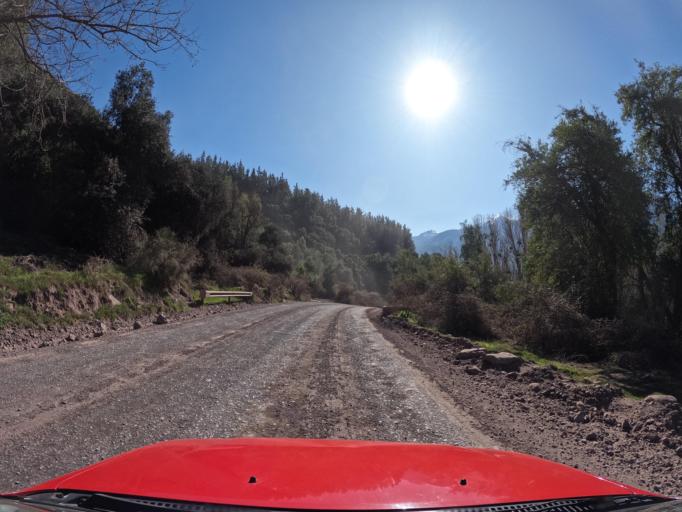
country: CL
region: O'Higgins
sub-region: Provincia de Colchagua
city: Chimbarongo
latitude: -35.0072
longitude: -70.7560
